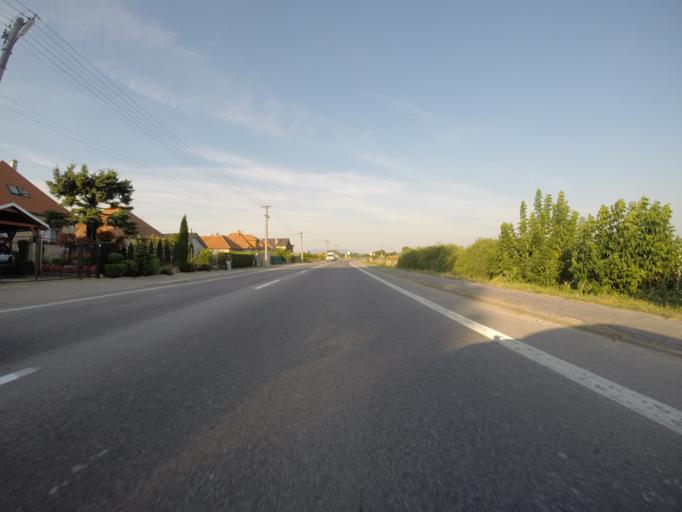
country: SK
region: Nitriansky
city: Banovce nad Bebravou
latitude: 48.6072
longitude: 18.2257
